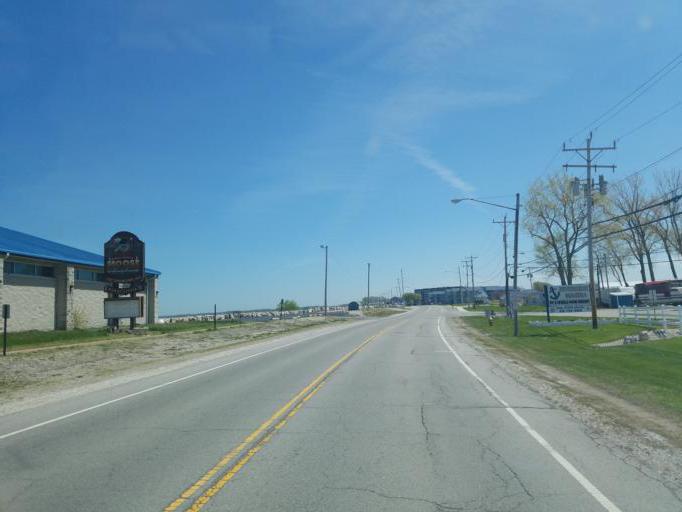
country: US
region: Ohio
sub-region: Ottawa County
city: Port Clinton
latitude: 41.5212
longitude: -82.9603
